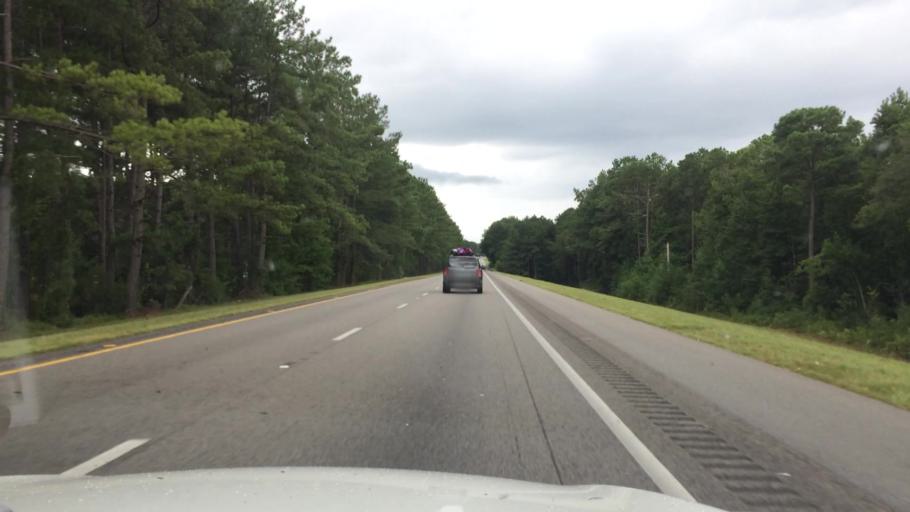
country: US
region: South Carolina
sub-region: Kershaw County
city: Camden
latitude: 34.2093
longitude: -80.4702
